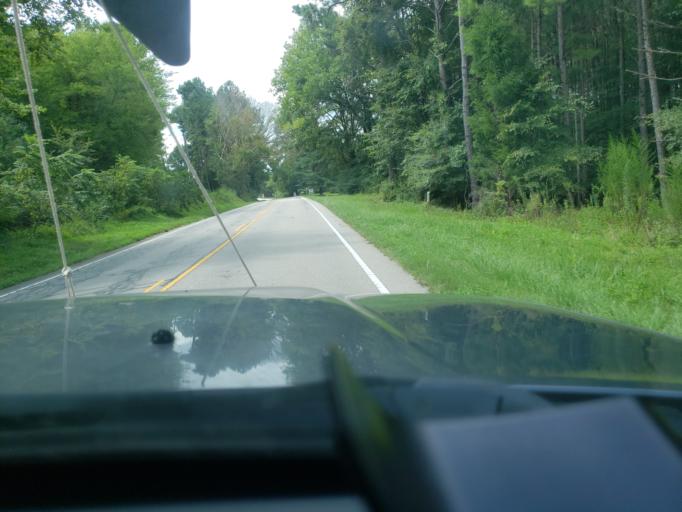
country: US
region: North Carolina
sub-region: Wake County
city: Rolesville
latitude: 35.8791
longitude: -78.4690
